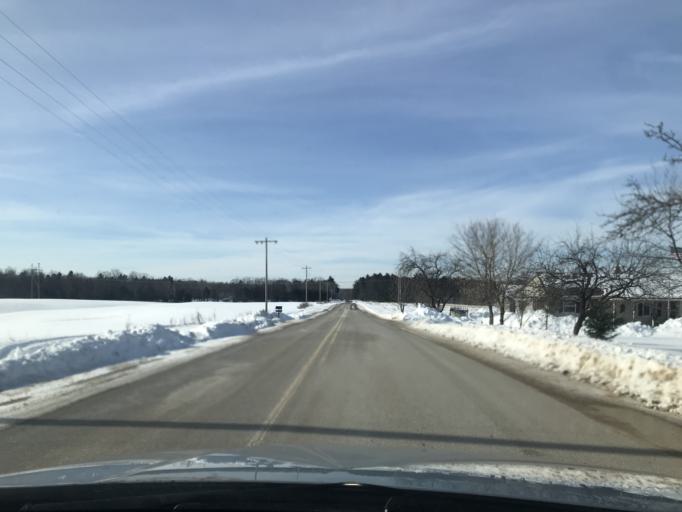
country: US
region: Wisconsin
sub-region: Oconto County
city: Oconto Falls
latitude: 45.1475
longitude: -88.1771
